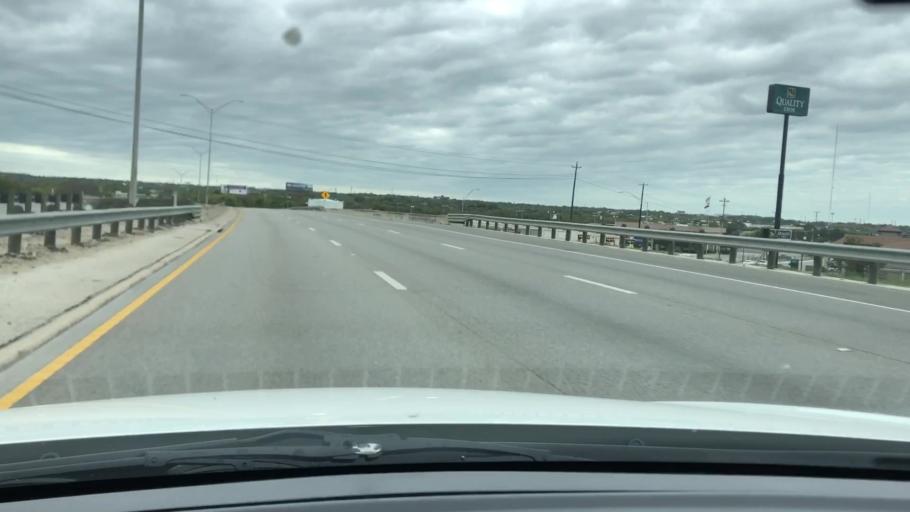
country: US
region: Texas
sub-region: Bexar County
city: Kirby
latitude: 29.4253
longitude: -98.4210
